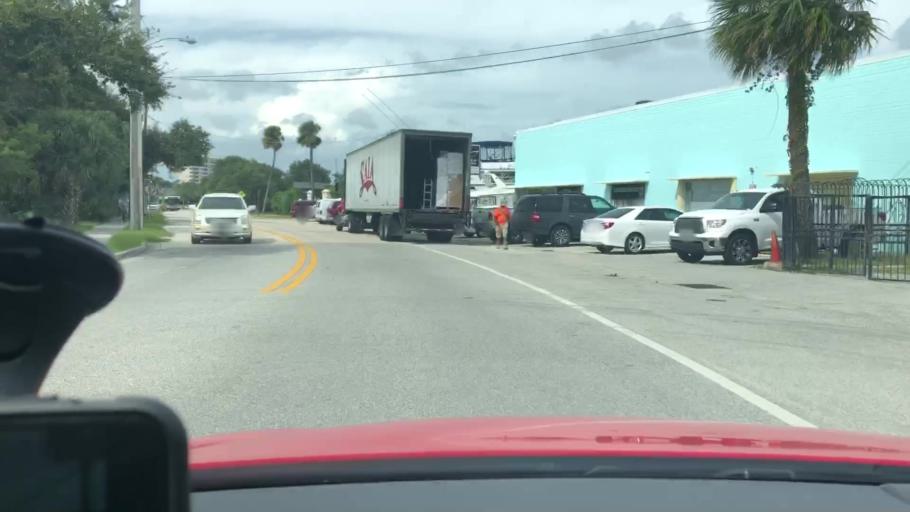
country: US
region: Florida
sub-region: Volusia County
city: Daytona Beach
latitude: 29.2005
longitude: -81.0140
